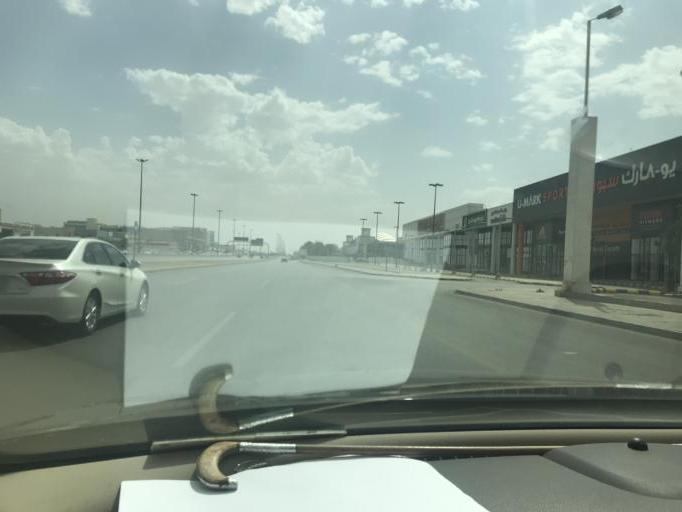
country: SA
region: Ar Riyad
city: Riyadh
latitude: 24.7257
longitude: 46.7792
